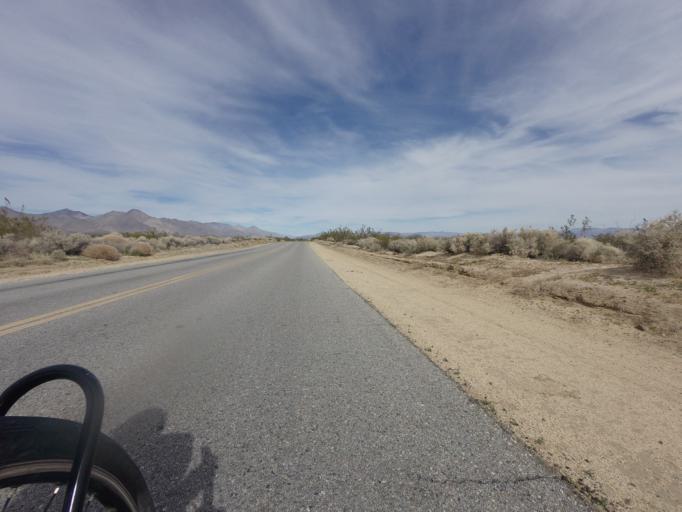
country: US
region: California
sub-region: Kern County
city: Inyokern
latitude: 35.7138
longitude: -117.8326
